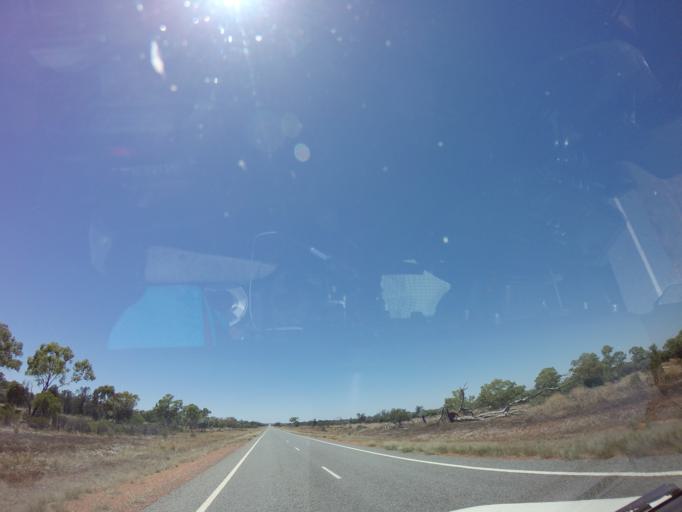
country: AU
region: New South Wales
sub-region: Cobar
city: Cobar
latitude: -31.5804
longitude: 144.8186
